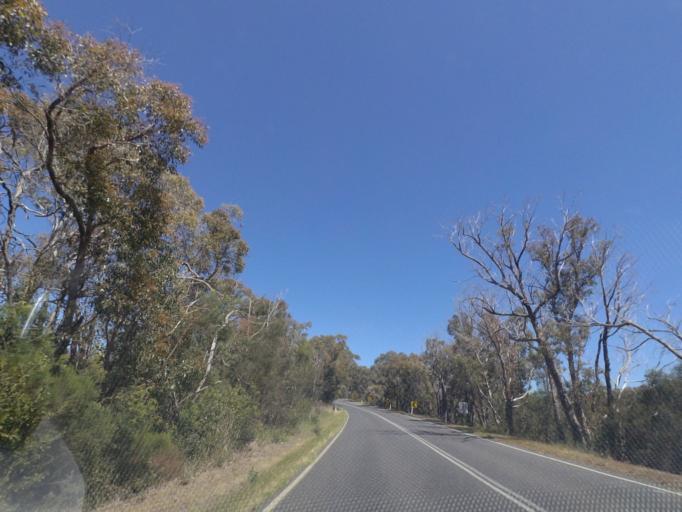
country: AU
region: Victoria
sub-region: Hume
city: Sunbury
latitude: -37.3039
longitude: 144.8605
